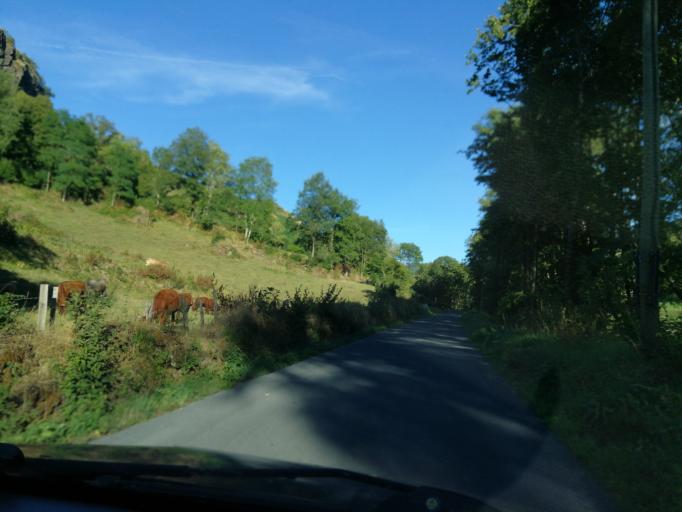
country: FR
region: Auvergne
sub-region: Departement du Cantal
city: Saint-Cernin
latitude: 45.1073
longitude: 2.5178
